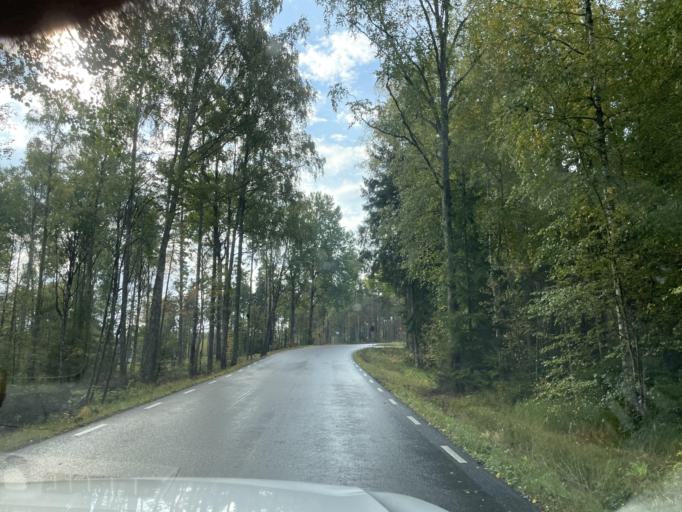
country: SE
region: Vaermland
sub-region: Karlstads Kommun
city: Skattkarr
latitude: 59.4039
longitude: 13.6030
